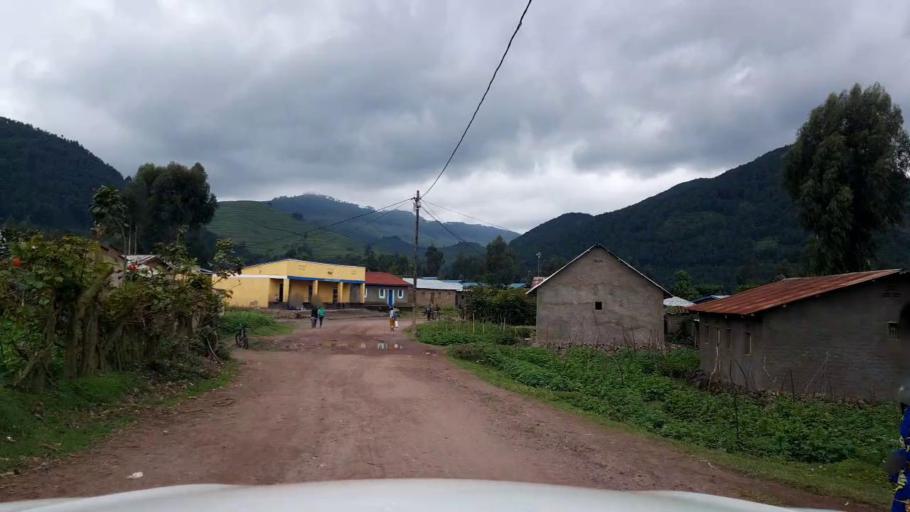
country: RW
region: Western Province
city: Gisenyi
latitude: -1.6389
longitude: 29.4071
